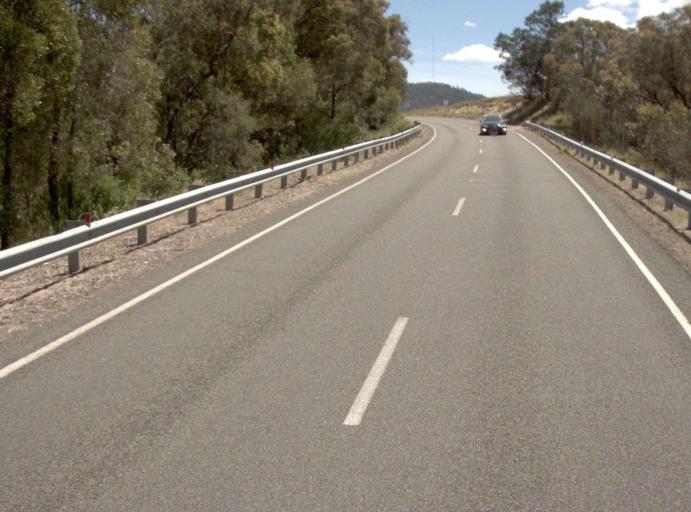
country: AU
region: Victoria
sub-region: Alpine
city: Mount Beauty
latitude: -37.1553
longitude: 147.6520
